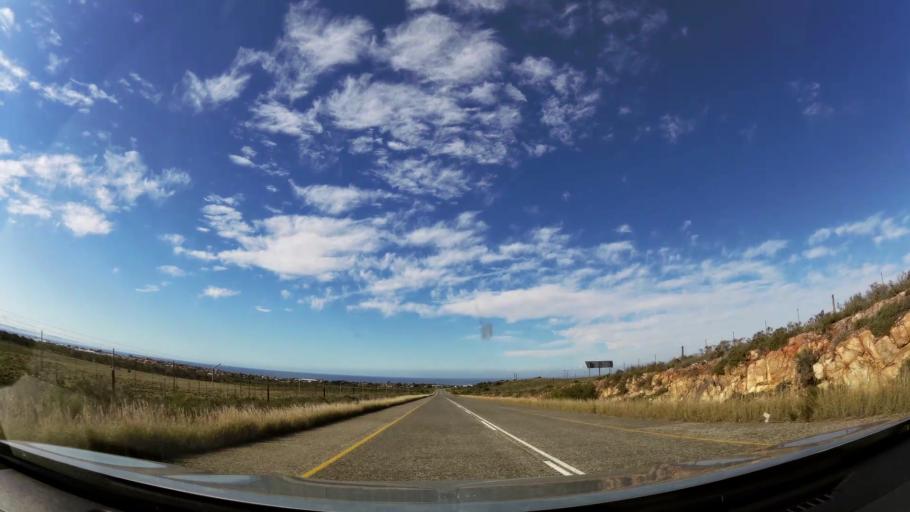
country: ZA
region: Eastern Cape
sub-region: Cacadu District Municipality
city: Jeffrey's Bay
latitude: -34.0218
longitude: 24.8940
